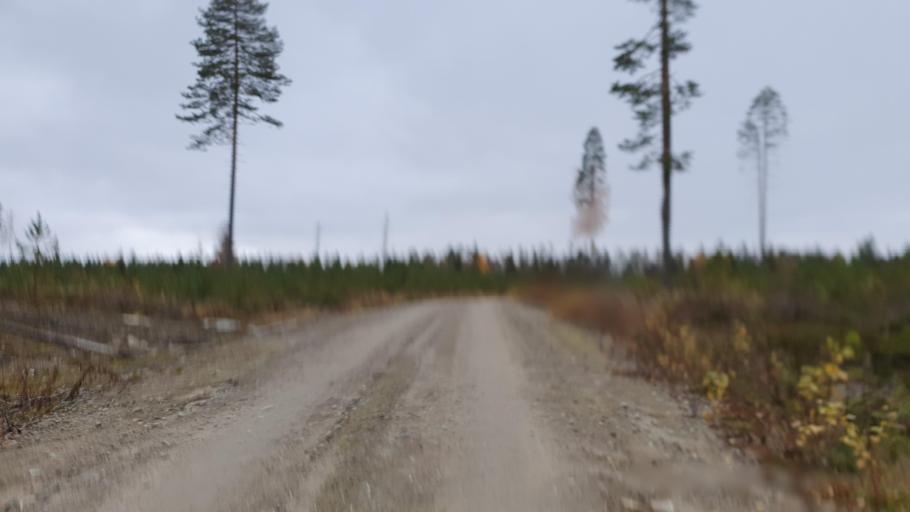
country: FI
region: Kainuu
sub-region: Kehys-Kainuu
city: Kuhmo
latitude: 64.4530
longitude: 29.6260
